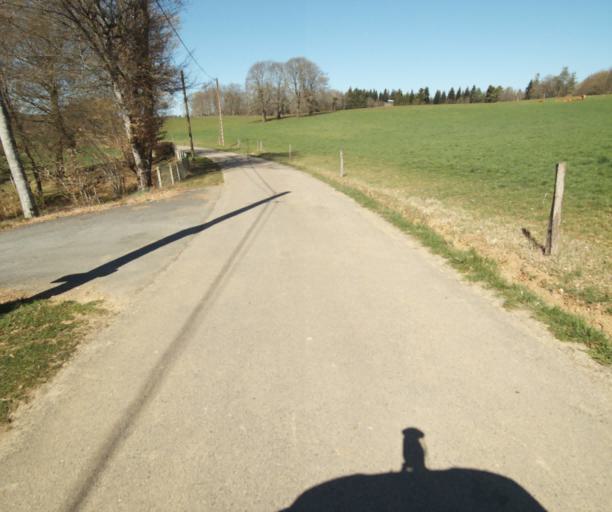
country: FR
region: Limousin
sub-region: Departement de la Correze
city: Saint-Clement
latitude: 45.3077
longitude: 1.7144
